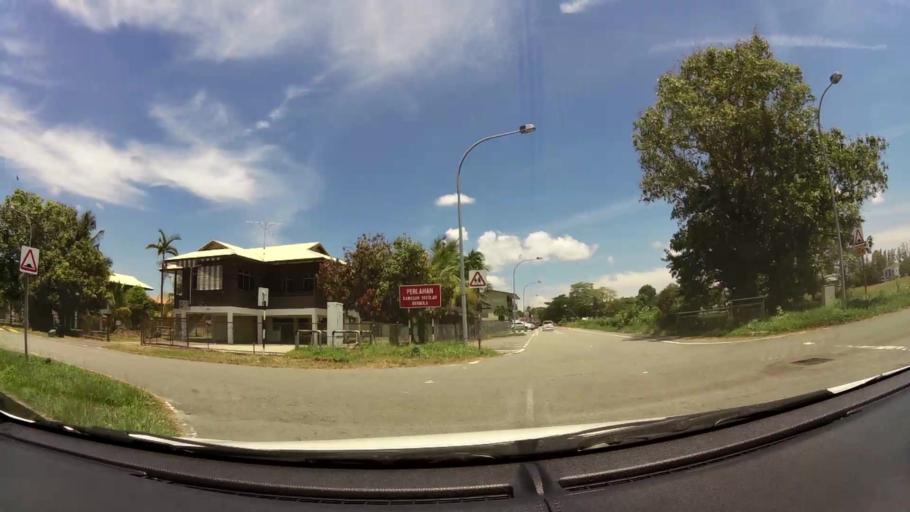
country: BN
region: Brunei and Muara
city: Bandar Seri Begawan
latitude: 4.9326
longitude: 114.9338
